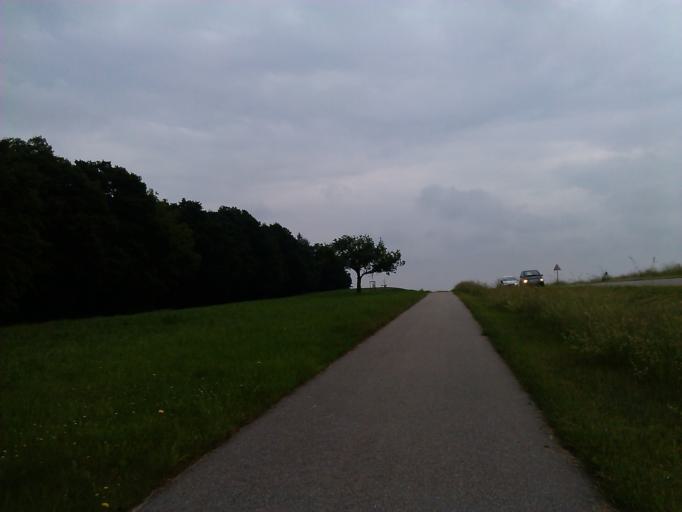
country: DE
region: Baden-Wuerttemberg
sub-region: Regierungsbezirk Stuttgart
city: Mainhardt
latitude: 49.0847
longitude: 9.5264
